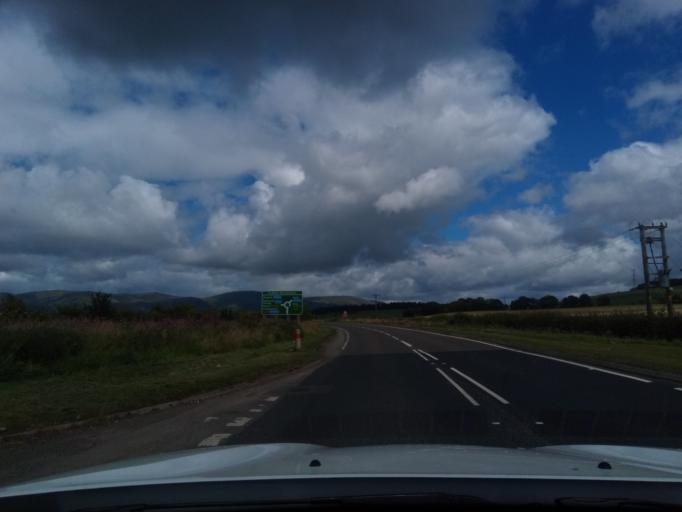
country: GB
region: Scotland
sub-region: Fife
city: Kincardine
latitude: 56.0935
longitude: -3.7181
